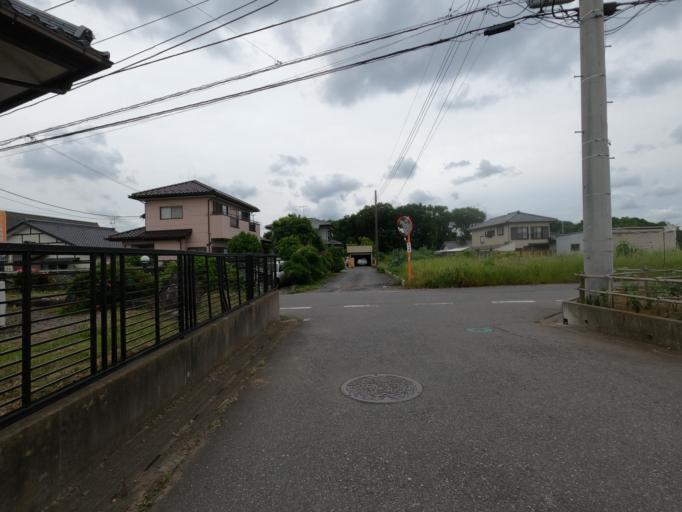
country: JP
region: Ibaraki
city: Moriya
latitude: 35.9505
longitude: 139.9712
